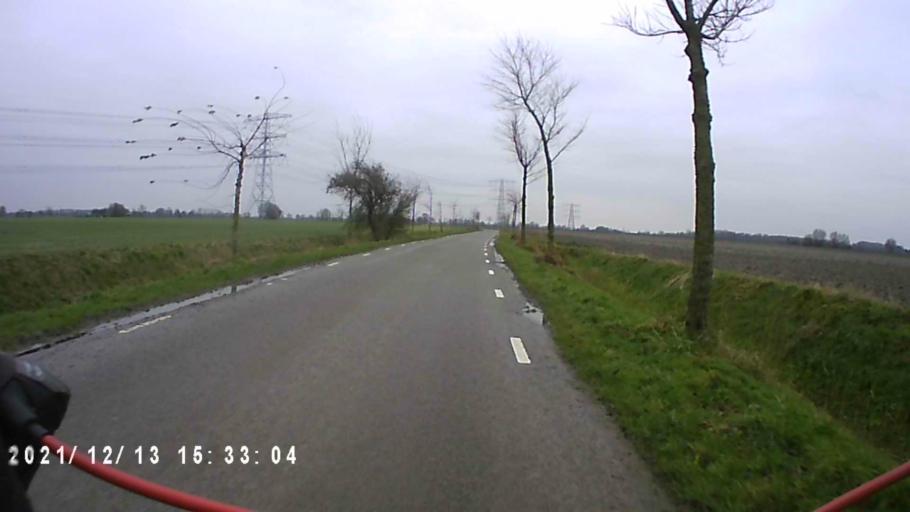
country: NL
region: Groningen
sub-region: Gemeente Appingedam
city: Appingedam
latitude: 53.3332
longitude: 6.8166
